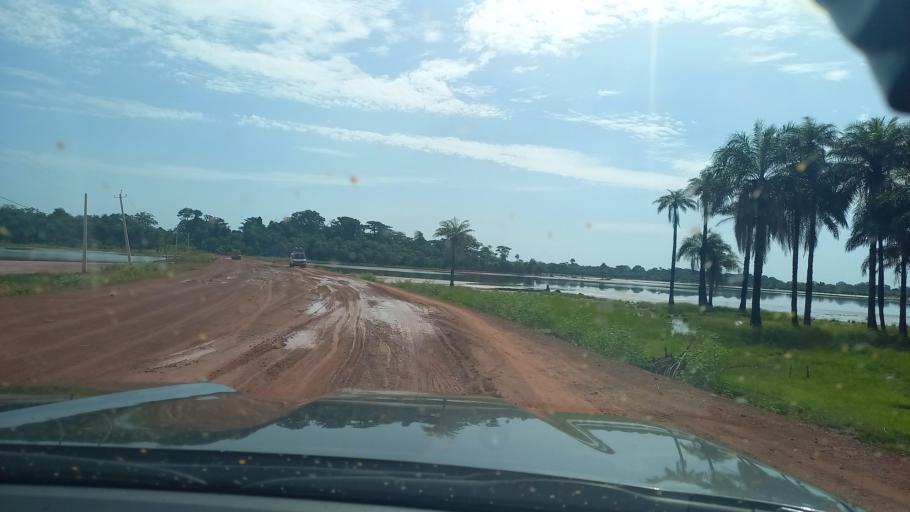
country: SN
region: Ziguinchor
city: Ziguinchor
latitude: 12.6734
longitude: -16.2040
